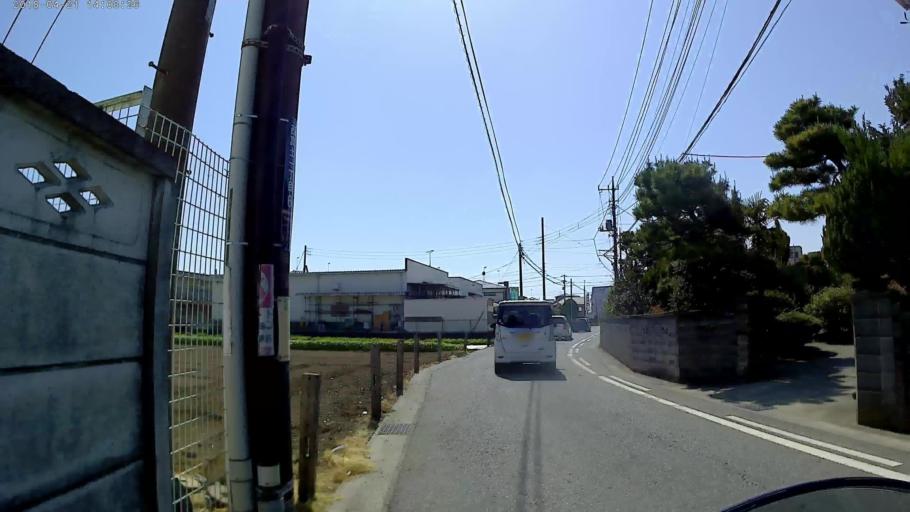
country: JP
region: Kanagawa
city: Hiratsuka
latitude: 35.3539
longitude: 139.3492
